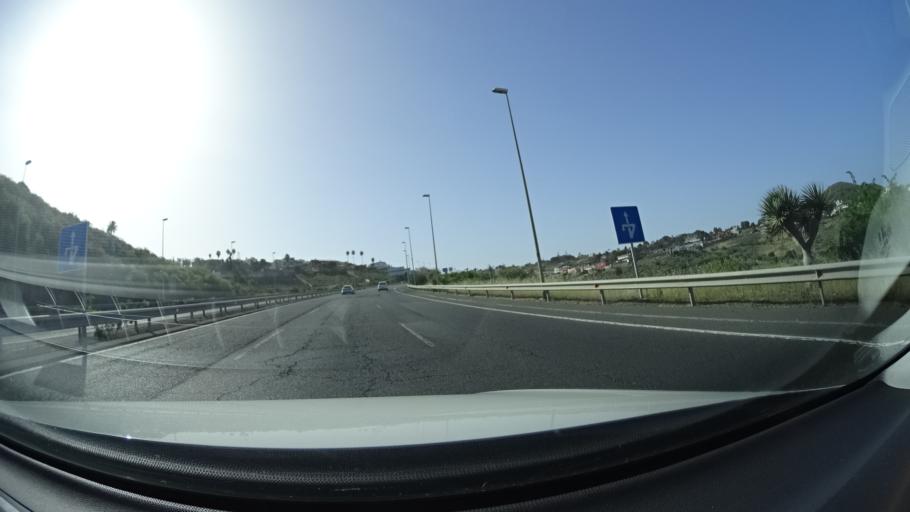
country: ES
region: Canary Islands
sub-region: Provincia de Las Palmas
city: Santa Brigida
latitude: 28.0494
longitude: -15.4530
